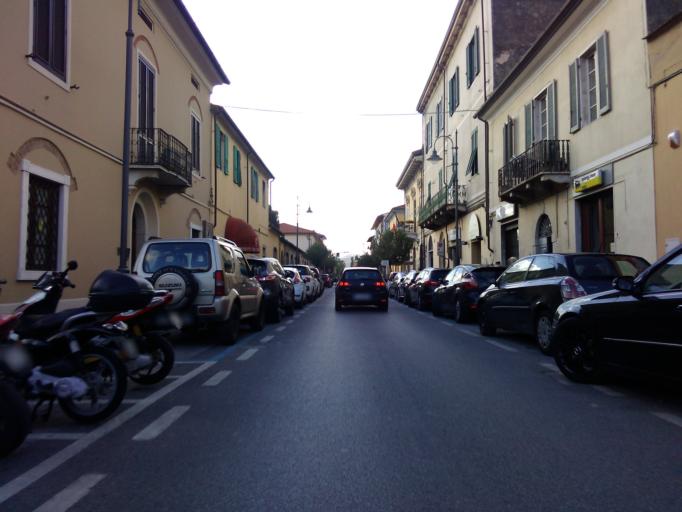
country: IT
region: Tuscany
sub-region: Provincia di Lucca
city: Pietrasanta
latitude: 43.9603
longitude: 10.2278
